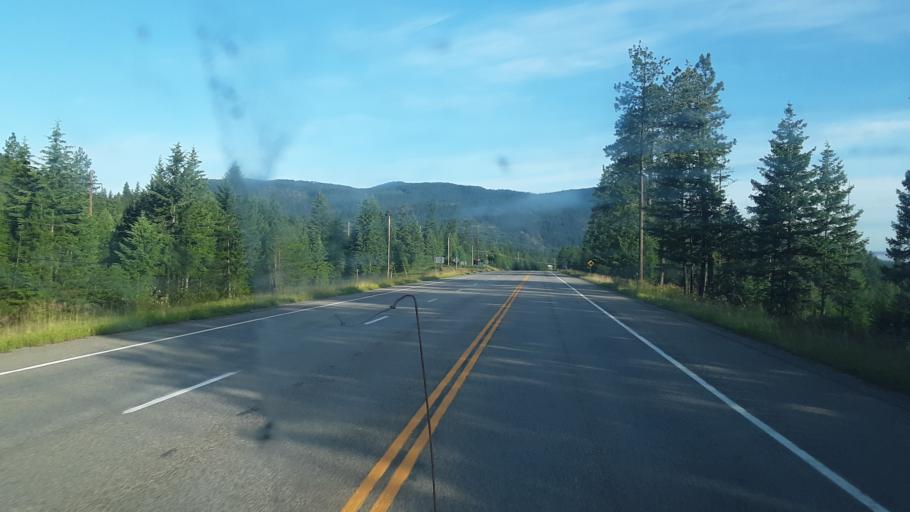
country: US
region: Montana
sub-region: Lincoln County
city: Libby
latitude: 48.4388
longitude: -115.8642
